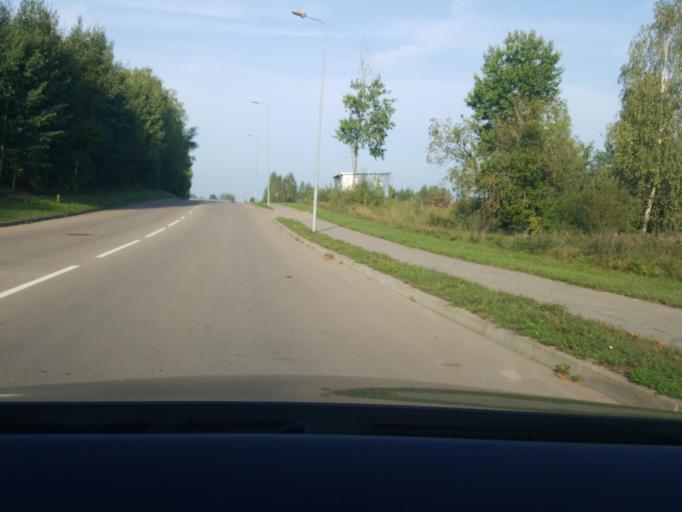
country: LT
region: Alytaus apskritis
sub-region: Alytus
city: Alytus
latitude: 54.4278
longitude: 24.0289
